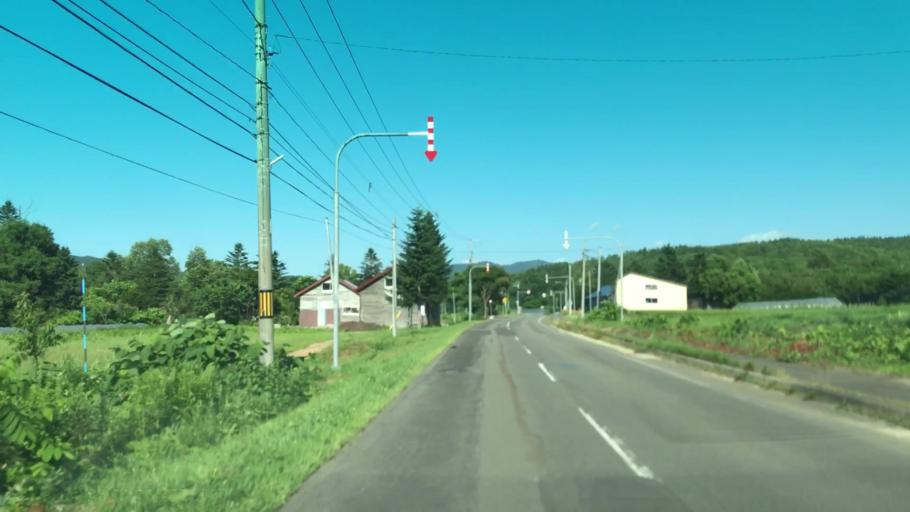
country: JP
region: Hokkaido
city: Yoichi
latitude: 43.0471
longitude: 140.8157
